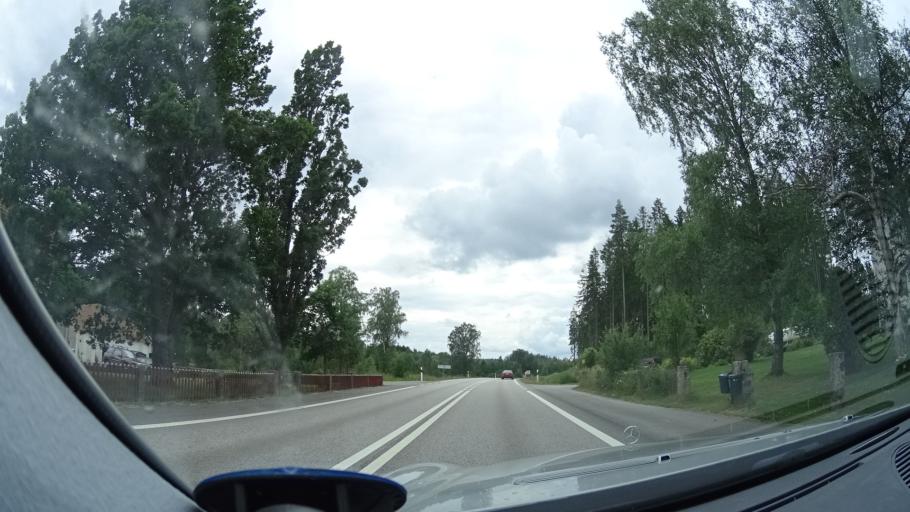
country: SE
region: Kronoberg
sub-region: Tingsryds Kommun
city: Tingsryd
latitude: 56.5017
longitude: 15.0425
